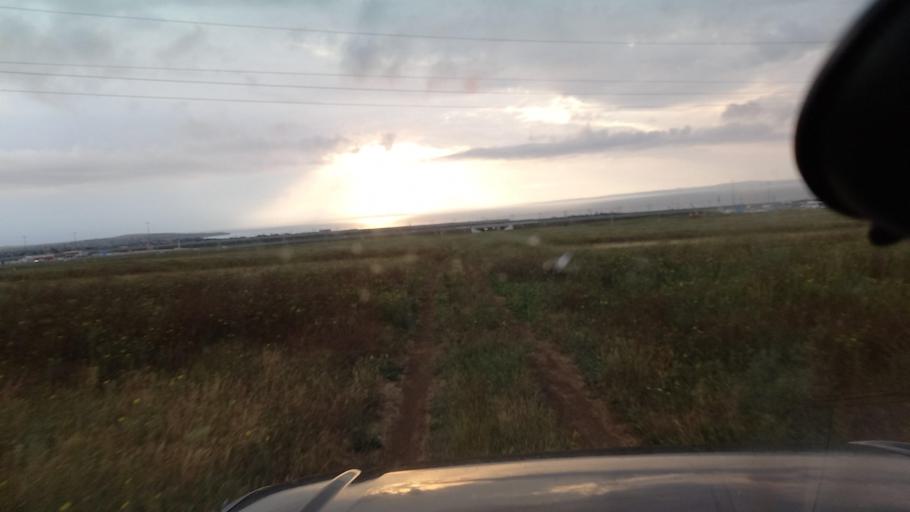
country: RU
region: Krasnodarskiy
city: Taman'
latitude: 45.2113
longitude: 36.7697
